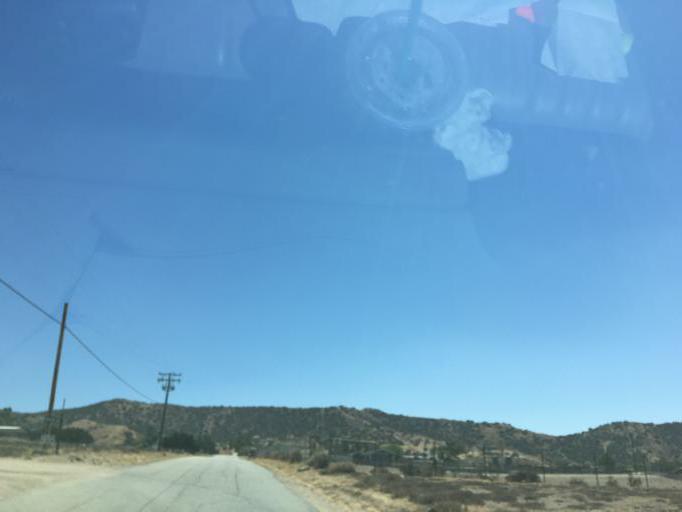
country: US
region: California
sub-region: Los Angeles County
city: Acton
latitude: 34.5245
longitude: -118.2283
